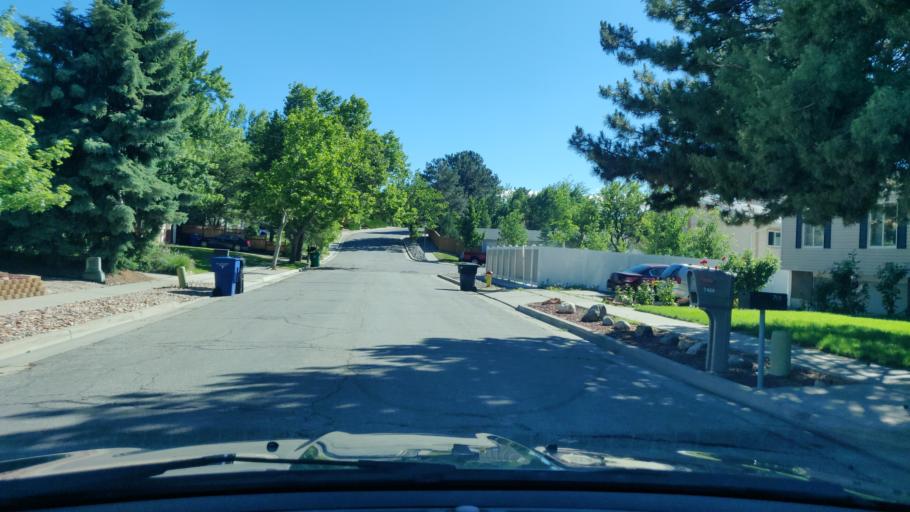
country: US
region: Utah
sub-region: Salt Lake County
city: Cottonwood Heights
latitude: 40.6152
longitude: -111.8083
